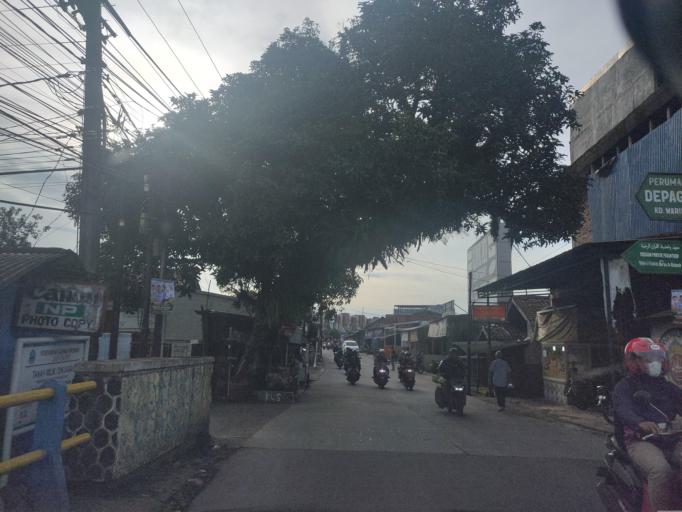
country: ID
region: West Java
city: Cibinong
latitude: -6.4997
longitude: 106.7931
